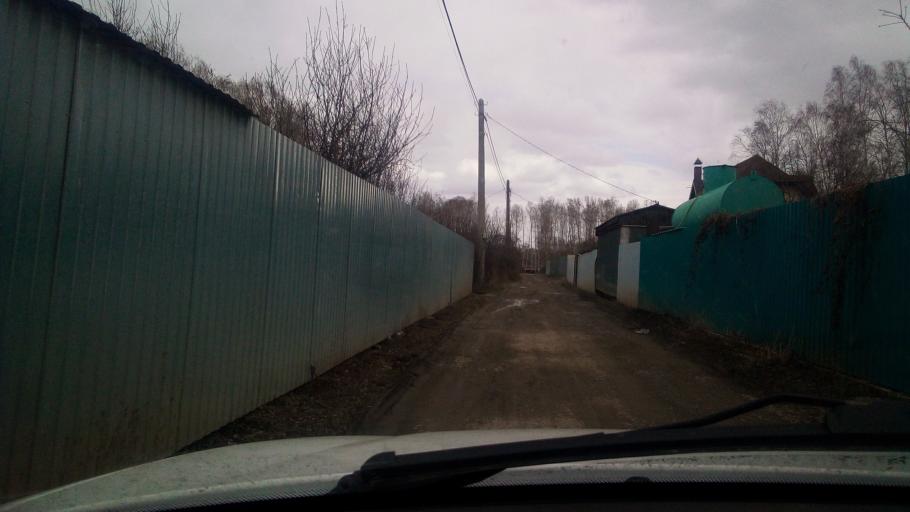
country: RU
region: Chelyabinsk
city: Sargazy
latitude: 55.1284
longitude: 61.2435
